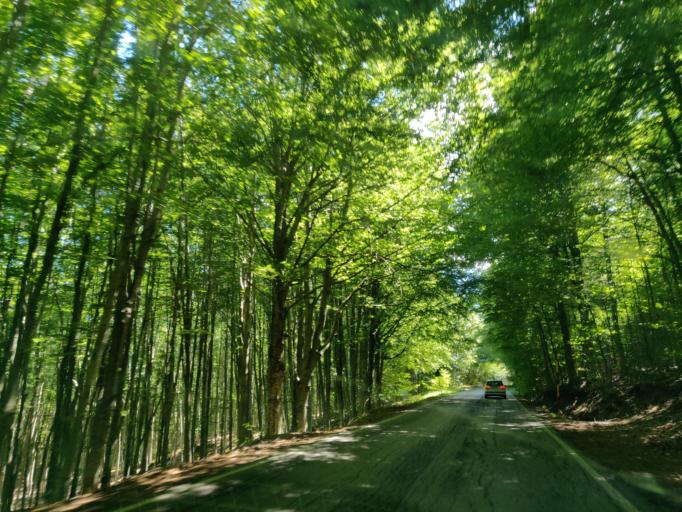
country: IT
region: Tuscany
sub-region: Provincia di Siena
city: Abbadia San Salvatore
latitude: 42.9030
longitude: 11.6228
